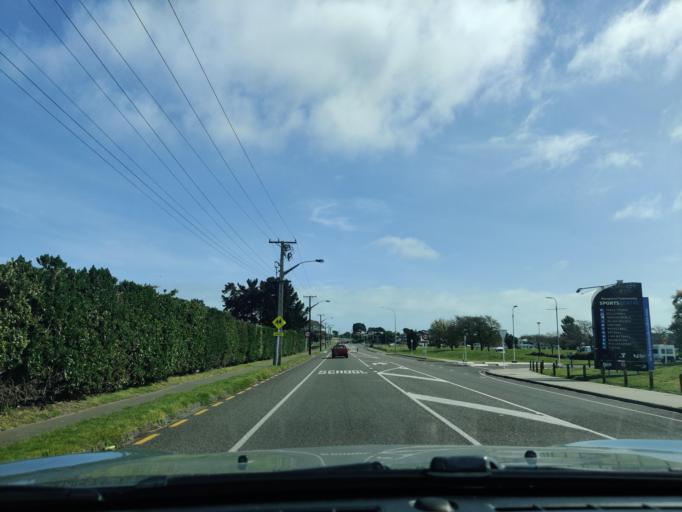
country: NZ
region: Manawatu-Wanganui
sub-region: Wanganui District
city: Wanganui
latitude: -39.9306
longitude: 175.0311
